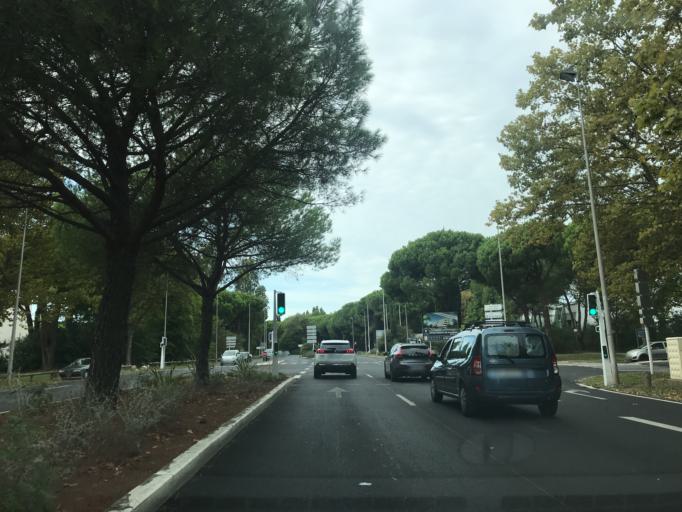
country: FR
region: Languedoc-Roussillon
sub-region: Departement de l'Herault
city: La Grande-Motte
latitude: 43.5612
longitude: 4.0966
